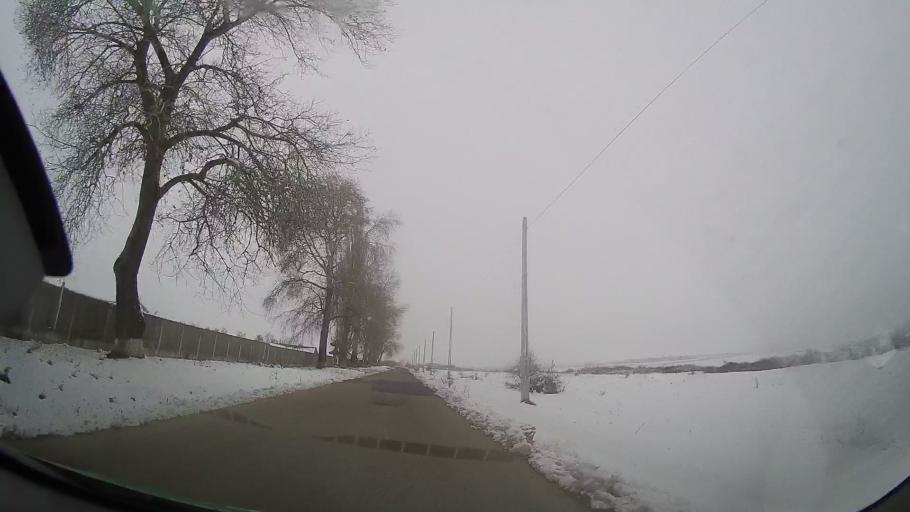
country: RO
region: Vaslui
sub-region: Comuna Todiresti
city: Todiresti
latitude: 46.8498
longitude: 27.3949
